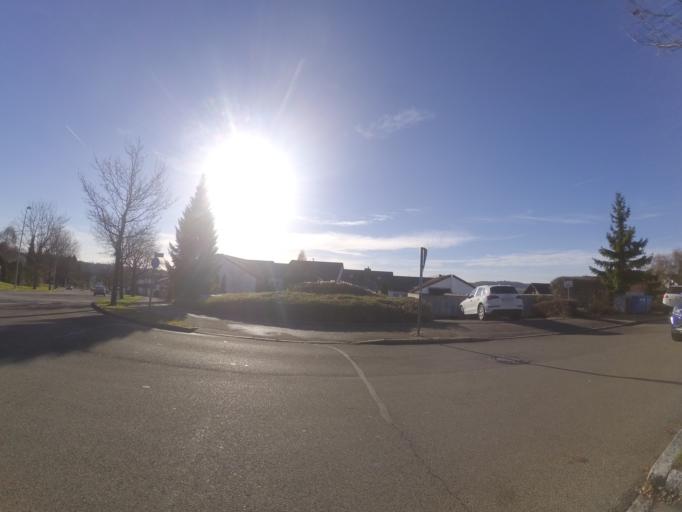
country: DE
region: Baden-Wuerttemberg
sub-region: Tuebingen Region
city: Ulm
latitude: 48.4101
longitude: 9.9471
